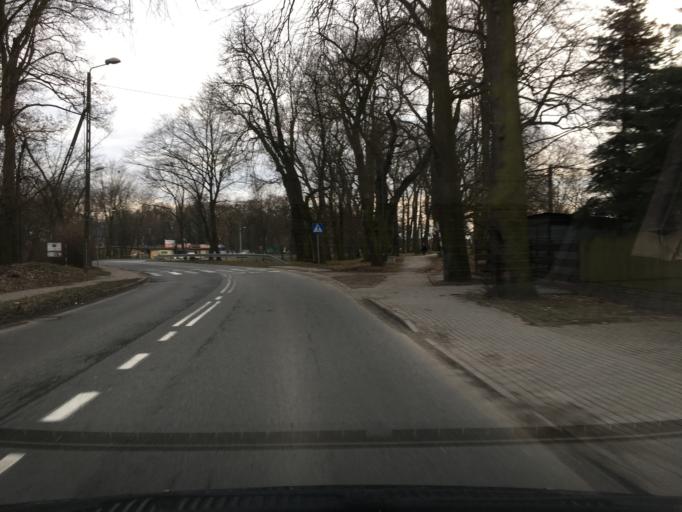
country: PL
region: Opole Voivodeship
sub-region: Powiat kedzierzynsko-kozielski
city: Kozle
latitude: 50.3304
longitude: 18.1499
